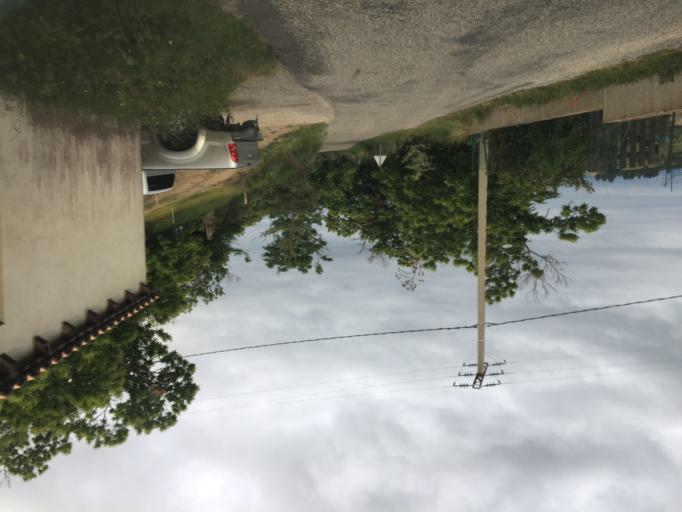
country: FR
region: Rhone-Alpes
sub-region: Departement de l'Ardeche
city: Saint-Julien-en-Saint-Alban
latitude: 44.7954
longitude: 4.6903
